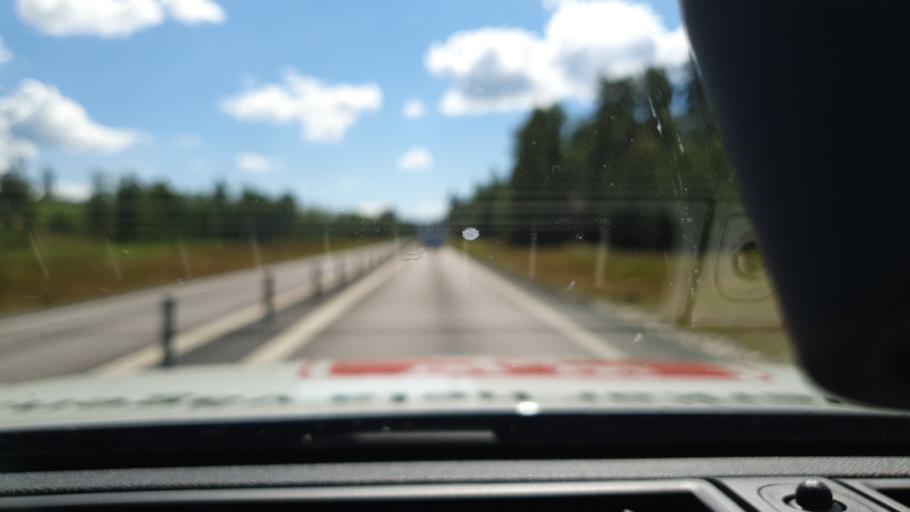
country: SE
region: Joenkoeping
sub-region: Aneby Kommun
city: Aneby
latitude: 57.8003
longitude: 14.8690
